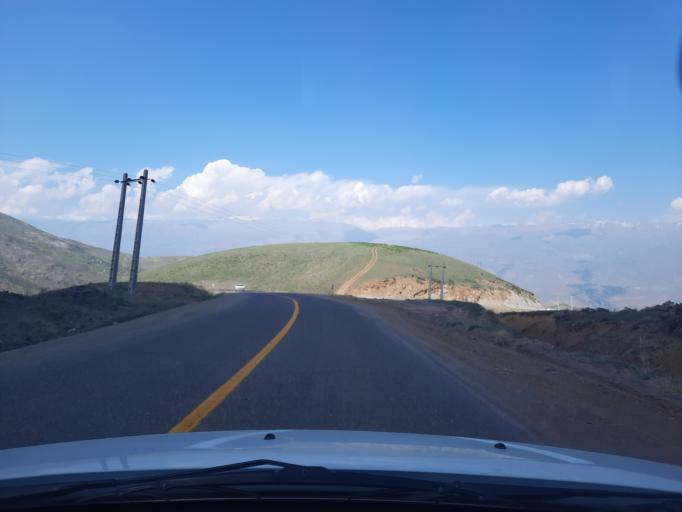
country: IR
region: Qazvin
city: Qazvin
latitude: 36.4008
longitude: 50.2202
